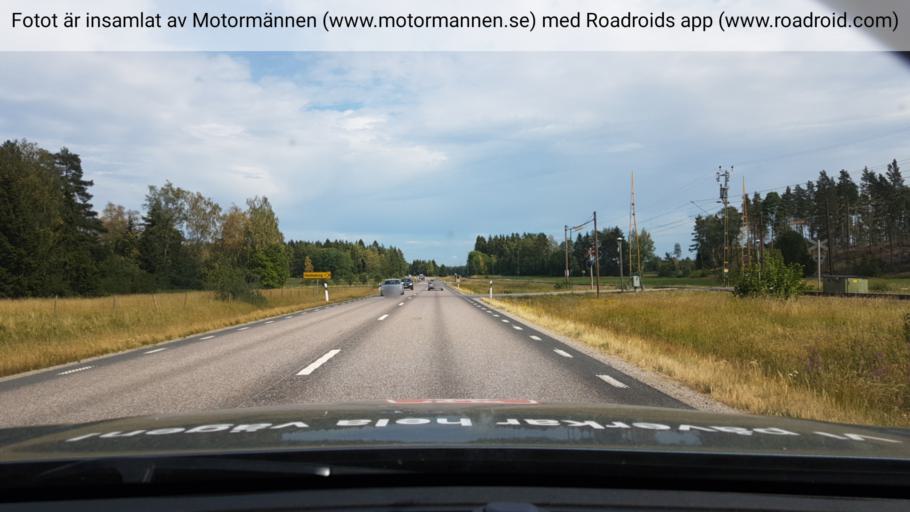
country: SE
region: Uppsala
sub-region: Enkopings Kommun
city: Orsundsbro
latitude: 59.8652
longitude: 17.3384
